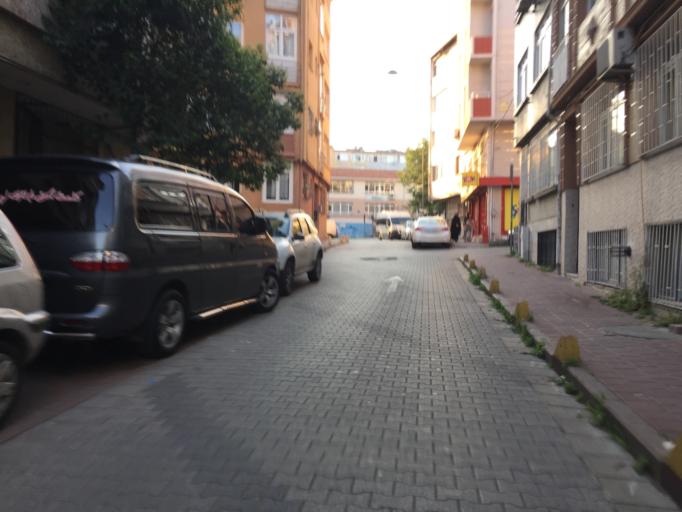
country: TR
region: Istanbul
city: Istanbul
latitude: 41.0205
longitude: 28.9401
